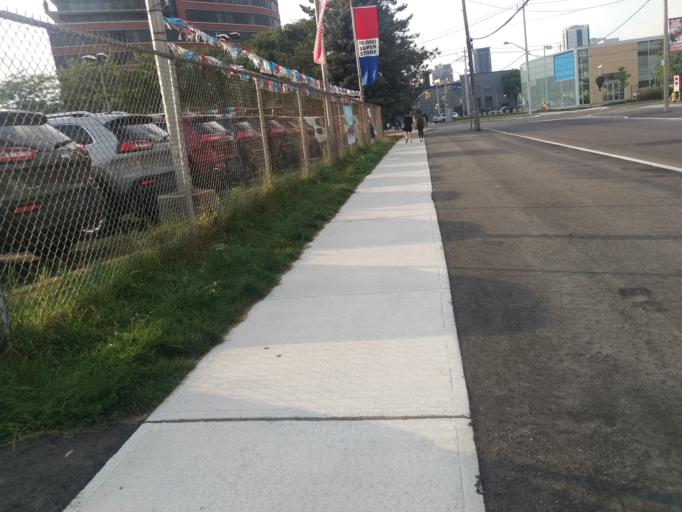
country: CA
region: Ontario
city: Toronto
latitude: 43.6516
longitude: -79.3602
